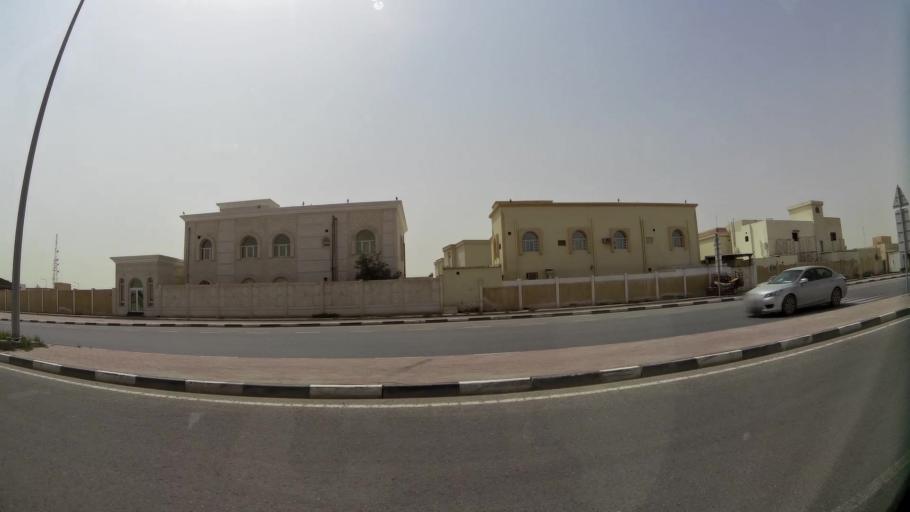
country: QA
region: Baladiyat ar Rayyan
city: Ar Rayyan
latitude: 25.2327
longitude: 51.4207
